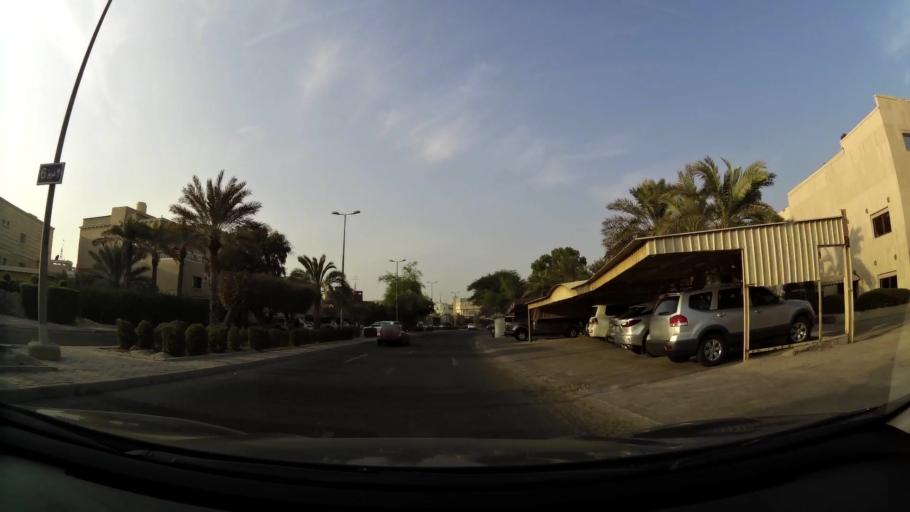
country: KW
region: Mubarak al Kabir
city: Sabah as Salim
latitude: 29.2562
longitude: 48.0702
